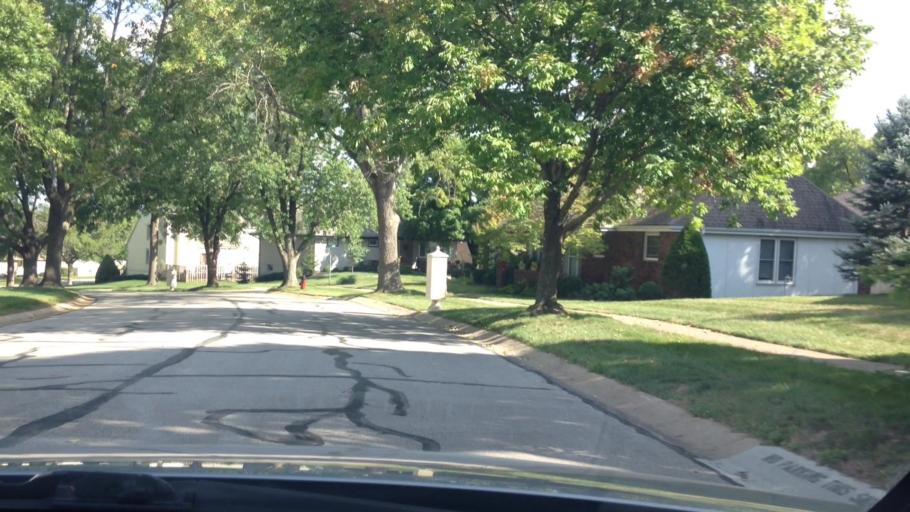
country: US
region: Missouri
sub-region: Jackson County
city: Grandview
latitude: 38.8929
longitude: -94.5934
